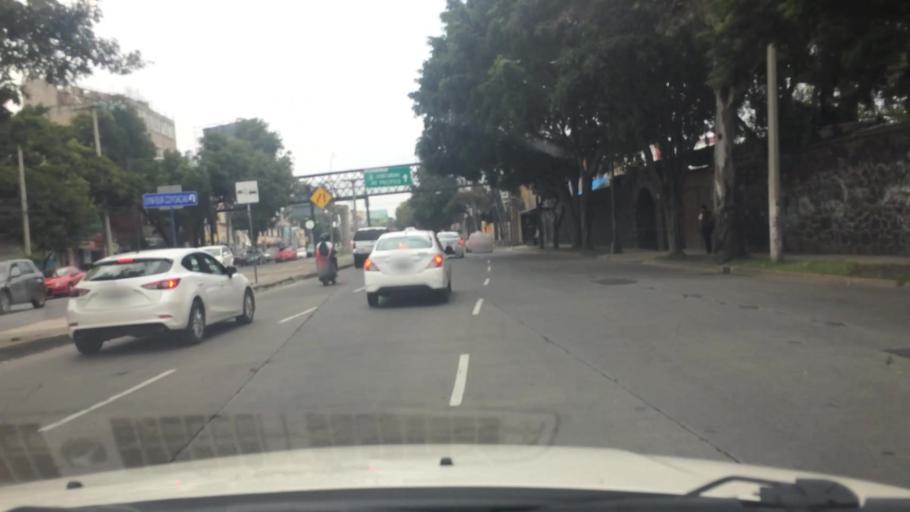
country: MX
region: Mexico City
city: Coyoacan
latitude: 19.3219
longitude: -99.1390
